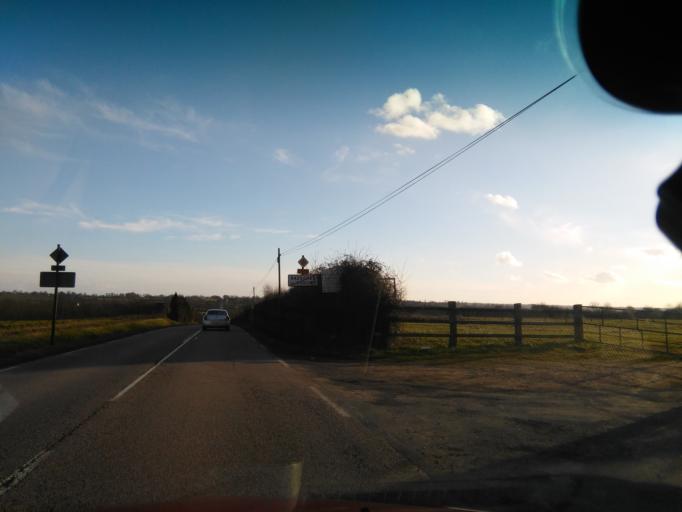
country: FR
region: Lower Normandy
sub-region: Departement de l'Orne
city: Pont-Ecrepin
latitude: 48.8111
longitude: -0.2421
